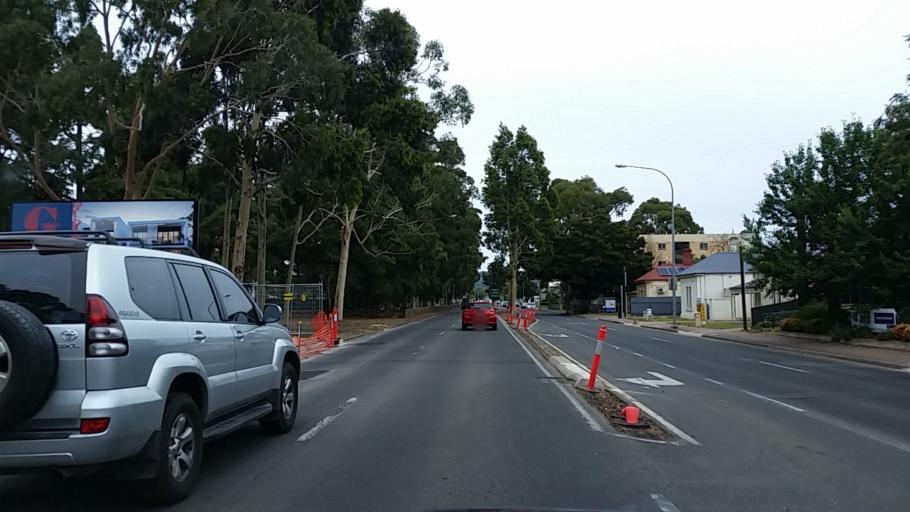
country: AU
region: South Australia
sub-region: Unley
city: Fullarton
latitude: -34.9432
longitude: 138.6248
